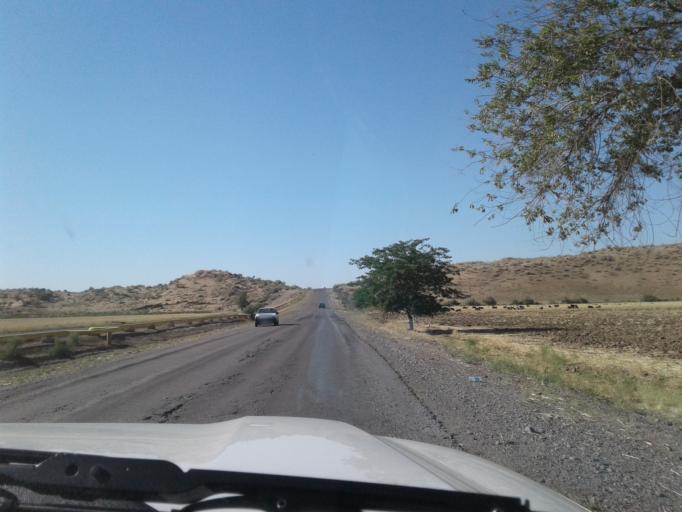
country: TM
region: Mary
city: Yoloeten
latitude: 36.7009
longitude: 62.4578
